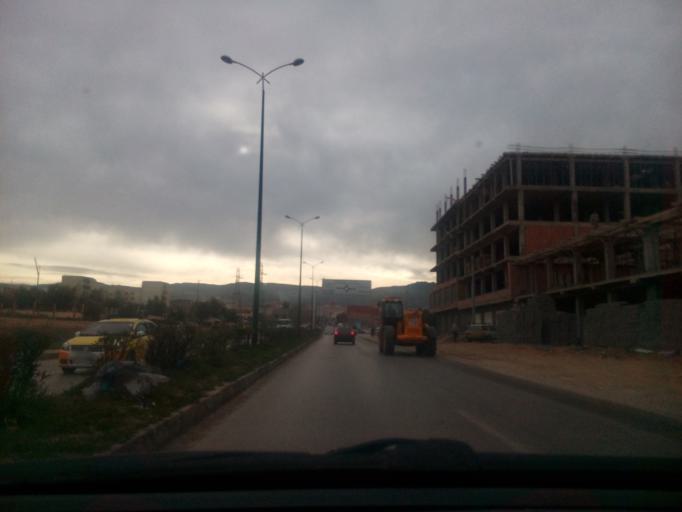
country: DZ
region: Tlemcen
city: Mansoura
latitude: 34.8861
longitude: -1.3532
